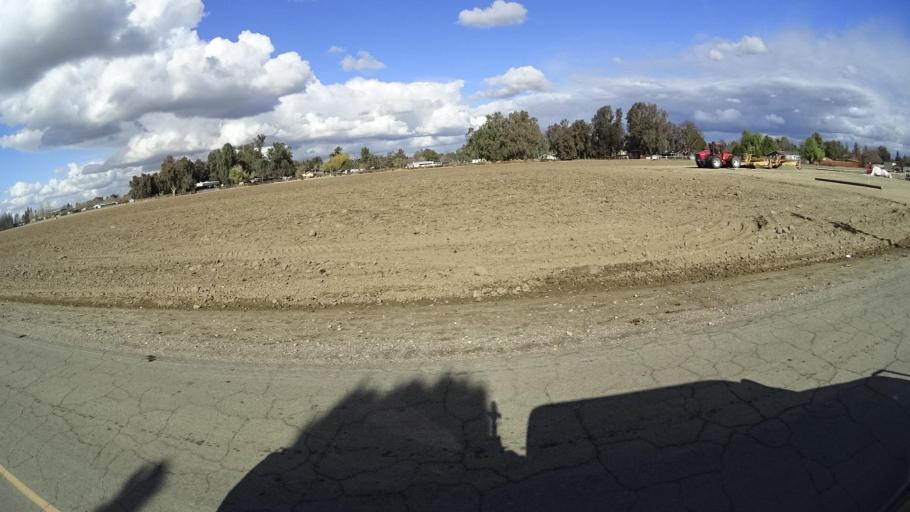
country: US
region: California
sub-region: Kern County
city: Greenfield
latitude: 35.2234
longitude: -119.0874
